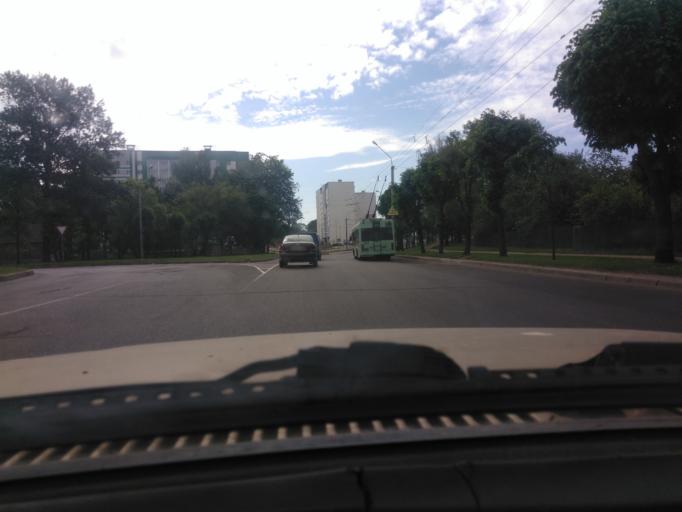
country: BY
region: Mogilev
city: Buynichy
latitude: 53.8975
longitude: 30.2945
